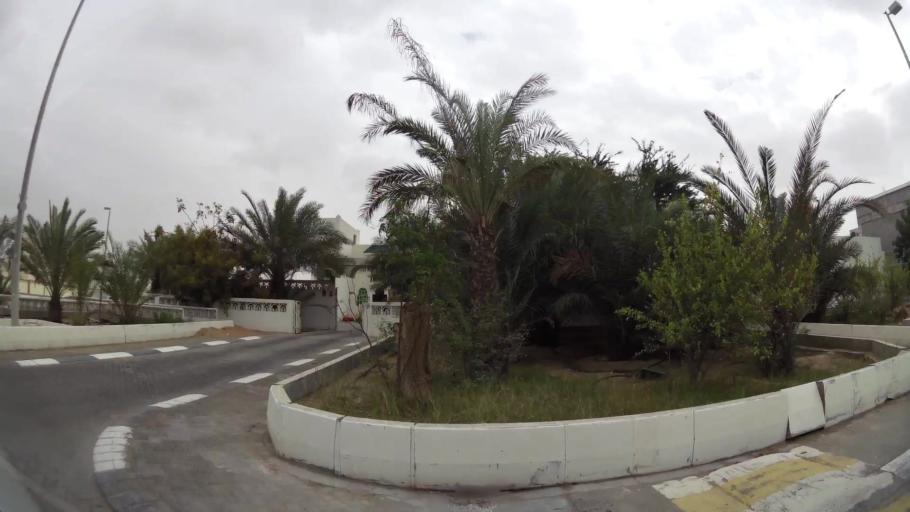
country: AE
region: Abu Dhabi
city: Abu Dhabi
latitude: 24.3447
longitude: 54.6457
